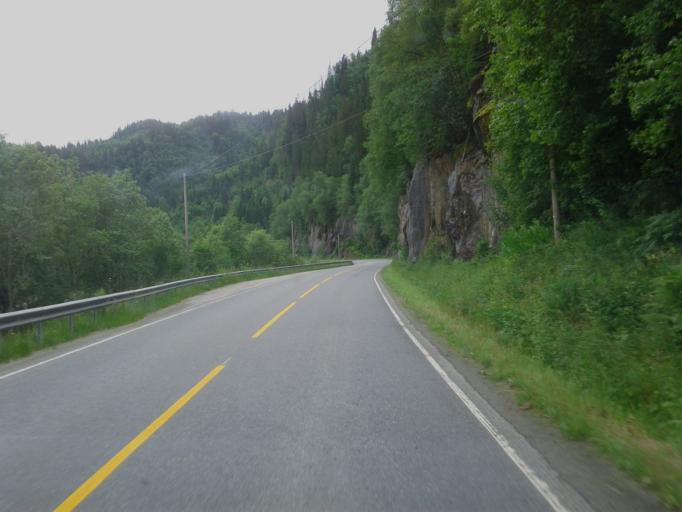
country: NO
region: Sor-Trondelag
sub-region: Midtre Gauldal
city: Storen
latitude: 62.9959
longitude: 10.4673
